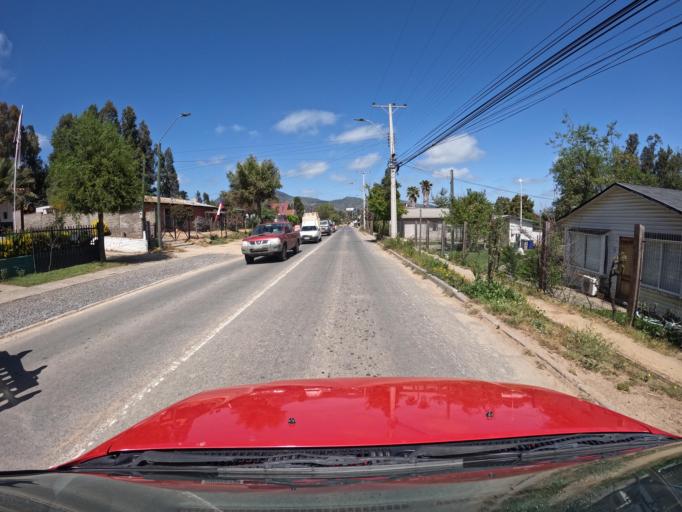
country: CL
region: O'Higgins
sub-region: Provincia de Colchagua
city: Santa Cruz
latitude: -34.7244
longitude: -71.6406
